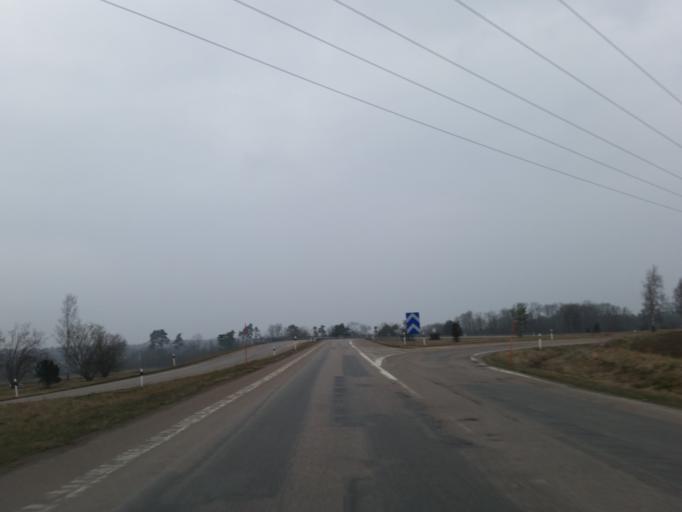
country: SE
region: Kalmar
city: Faerjestaden
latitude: 56.6701
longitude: 16.5157
